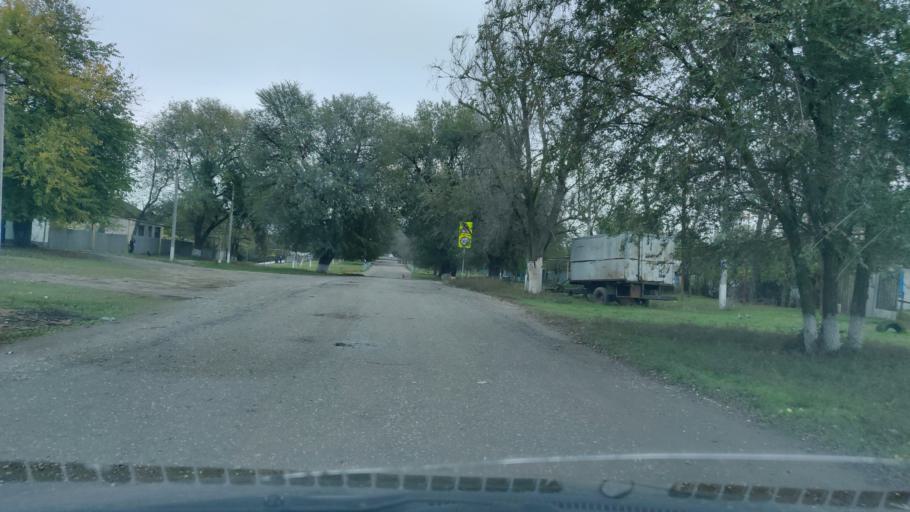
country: RU
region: Stavropol'skiy
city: Irgakly
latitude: 44.2456
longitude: 44.7193
